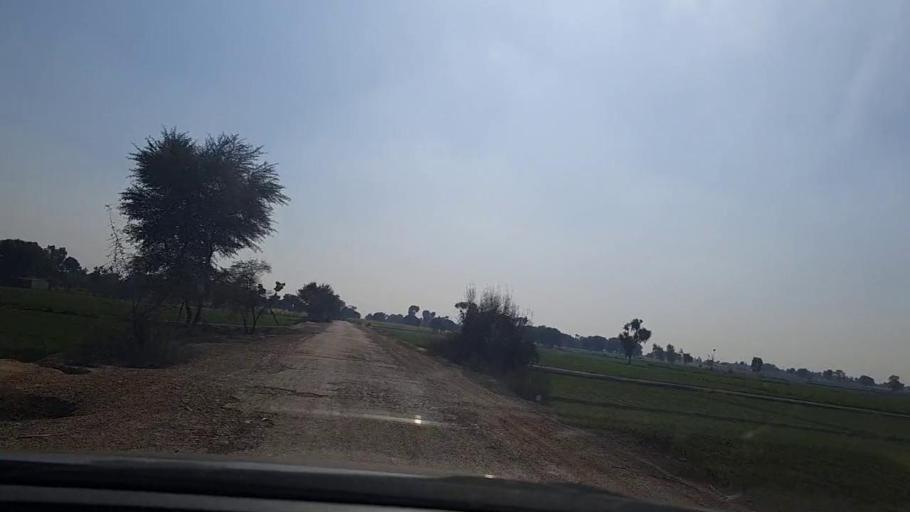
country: PK
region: Sindh
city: Daulatpur
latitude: 26.2874
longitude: 68.0678
